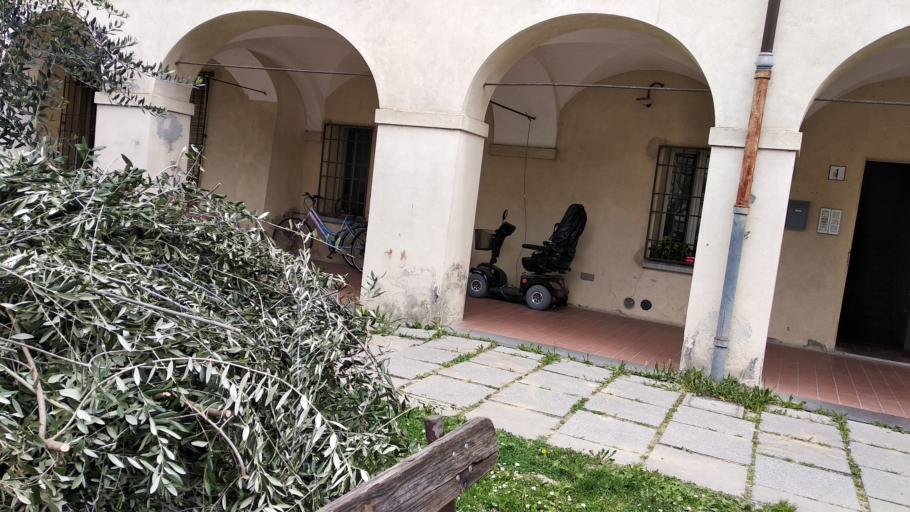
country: IT
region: Emilia-Romagna
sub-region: Provincia di Ravenna
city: Brisighella
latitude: 44.2222
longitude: 11.7697
